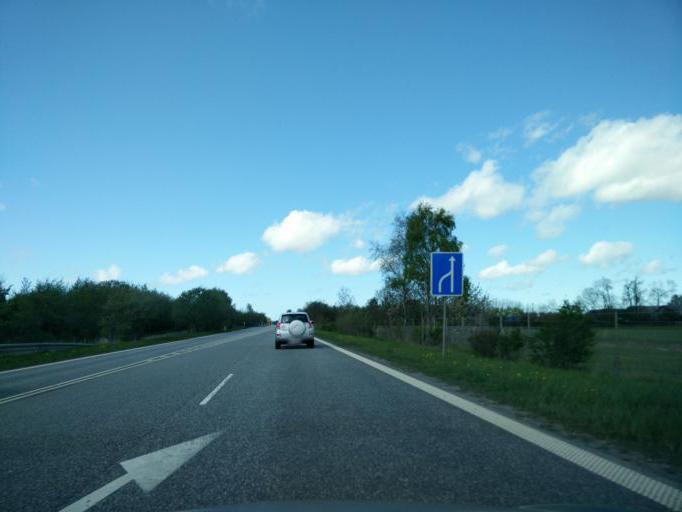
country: DK
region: Capital Region
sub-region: Hillerod Kommune
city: Hillerod
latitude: 55.9213
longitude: 12.2594
